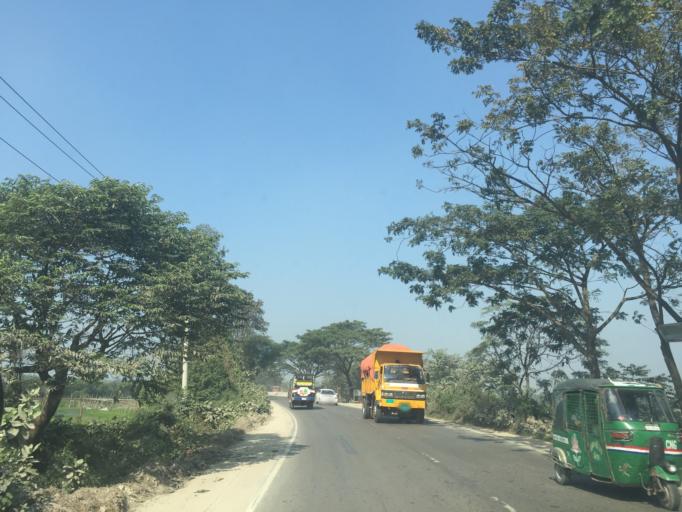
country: BD
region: Dhaka
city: Tungi
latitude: 23.8428
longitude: 90.3429
